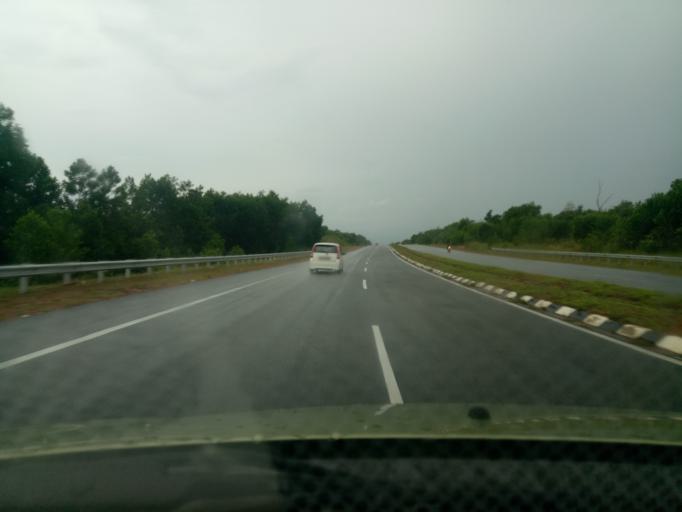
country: MY
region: Kedah
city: Sungai Petani
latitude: 5.6173
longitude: 100.5562
